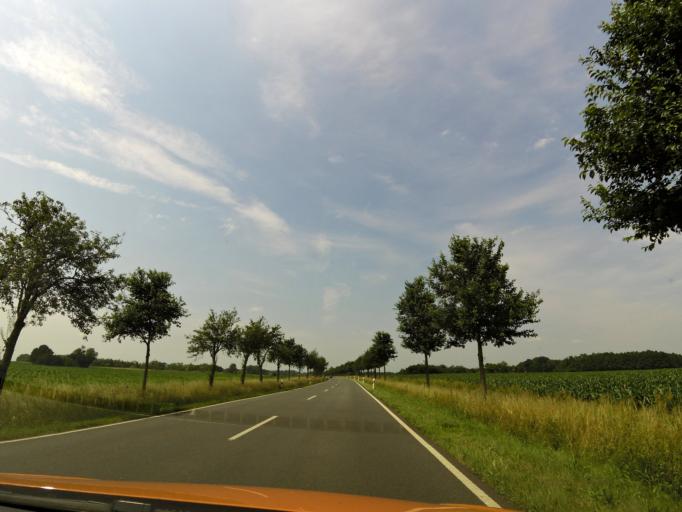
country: DE
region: Brandenburg
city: Kyritz
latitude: 52.9707
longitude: 12.3720
